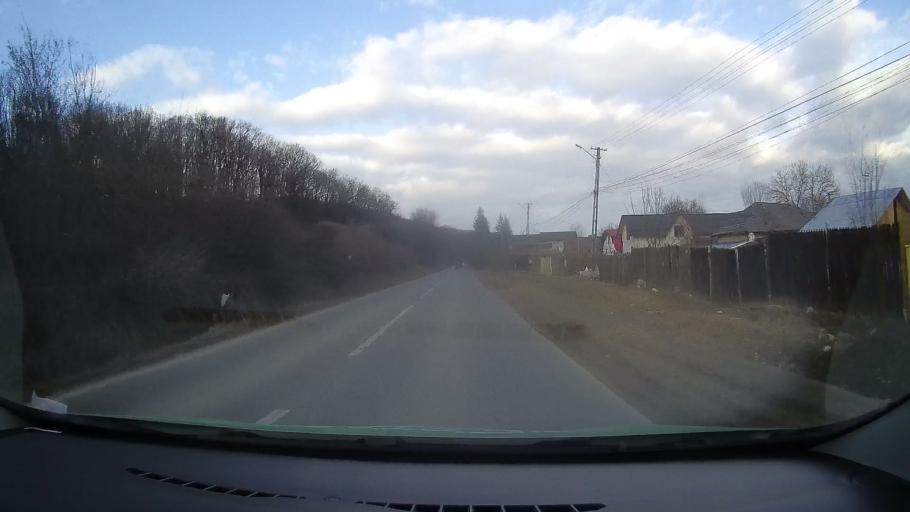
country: RO
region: Dambovita
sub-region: Comuna Gura Ocnitei
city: Gura Ocnitei
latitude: 44.9434
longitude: 25.5837
